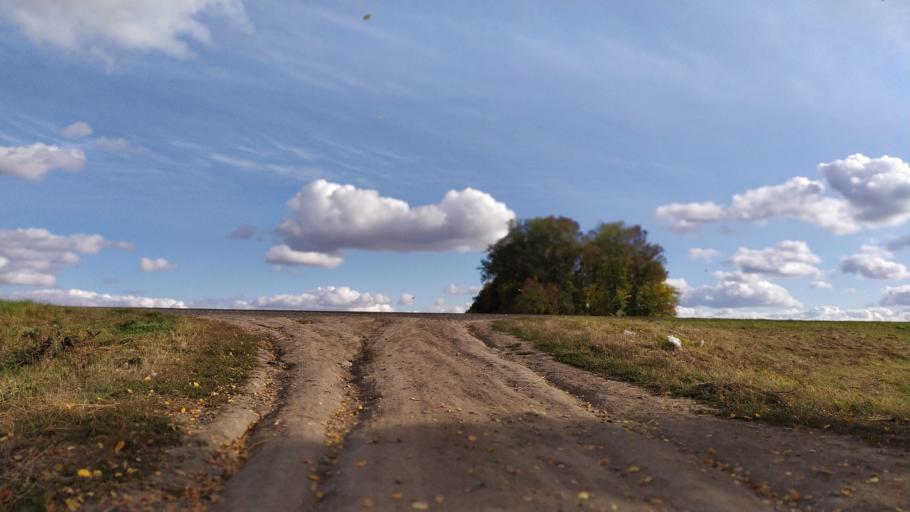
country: RU
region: Kursk
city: Kursk
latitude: 51.6152
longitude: 36.1647
